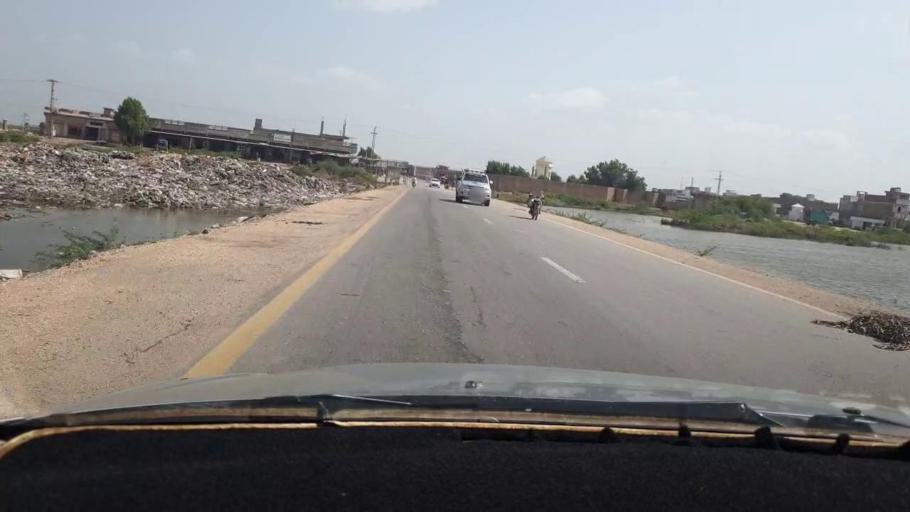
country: PK
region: Sindh
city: Digri
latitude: 25.1623
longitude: 69.1165
